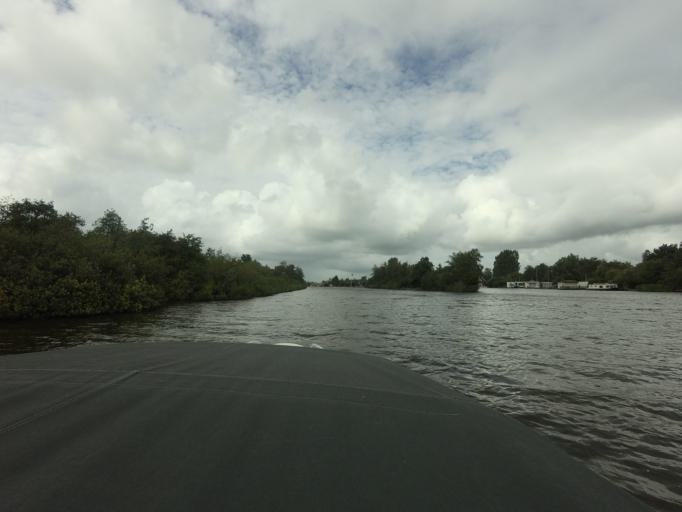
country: NL
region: Friesland
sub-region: Gemeente Tytsjerksteradiel
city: Garyp
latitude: 53.1216
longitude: 5.9432
